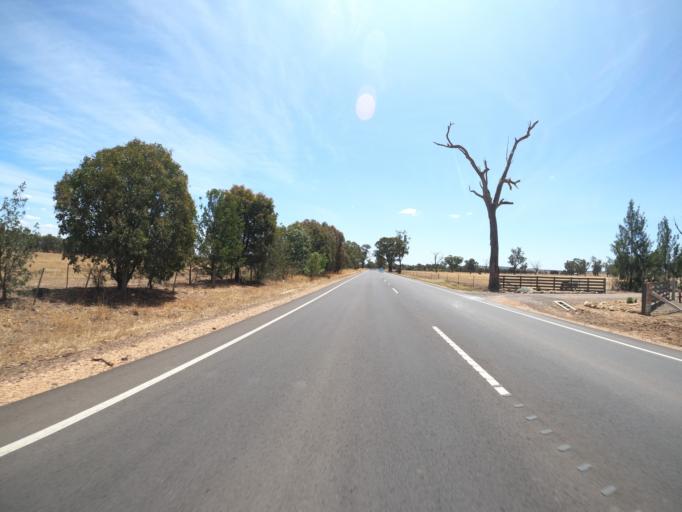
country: AU
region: Victoria
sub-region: Benalla
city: Benalla
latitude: -36.5026
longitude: 146.0233
